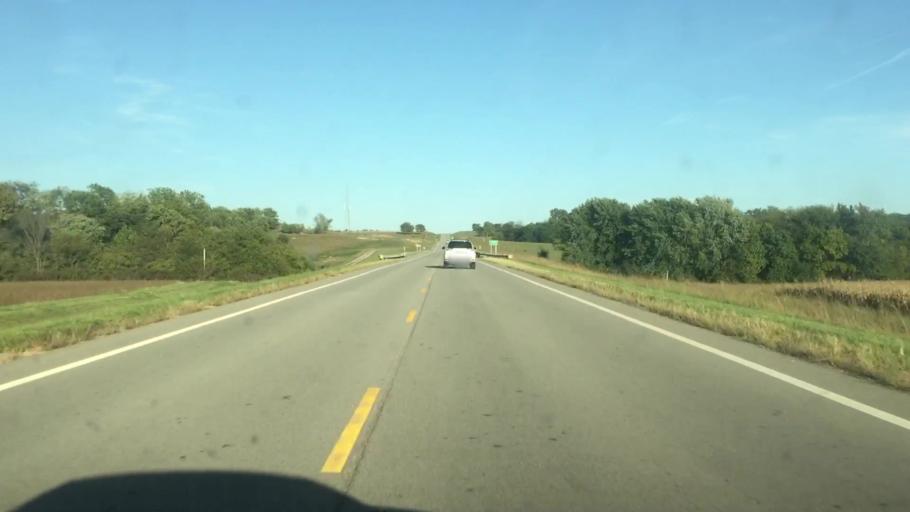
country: US
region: Kansas
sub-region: Brown County
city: Horton
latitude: 39.5875
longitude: -95.5575
